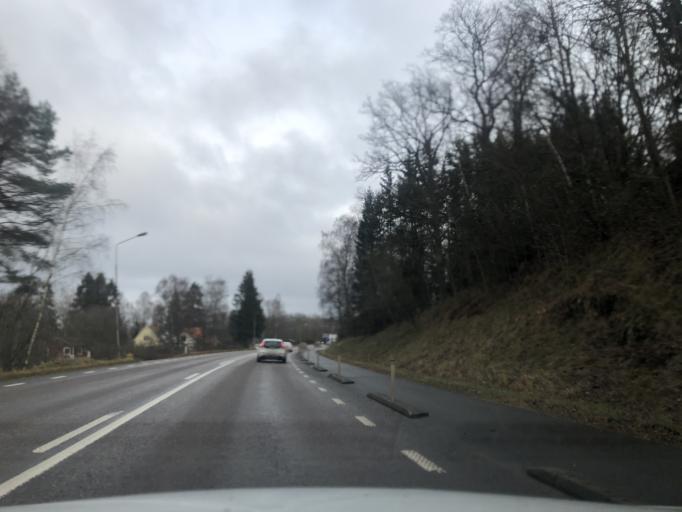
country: SE
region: Vaestra Goetaland
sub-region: Ulricehamns Kommun
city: Ulricehamn
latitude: 57.8187
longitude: 13.4214
